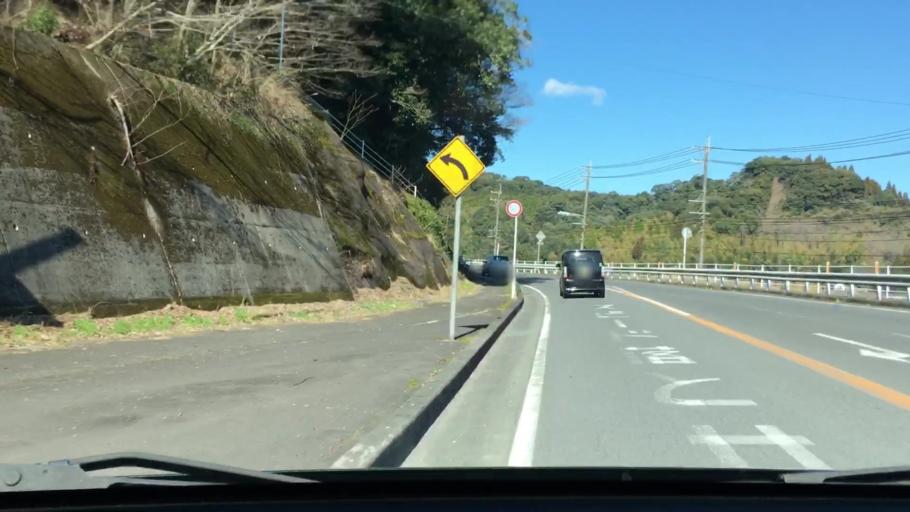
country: JP
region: Kagoshima
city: Ijuin
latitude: 31.6580
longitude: 130.4957
